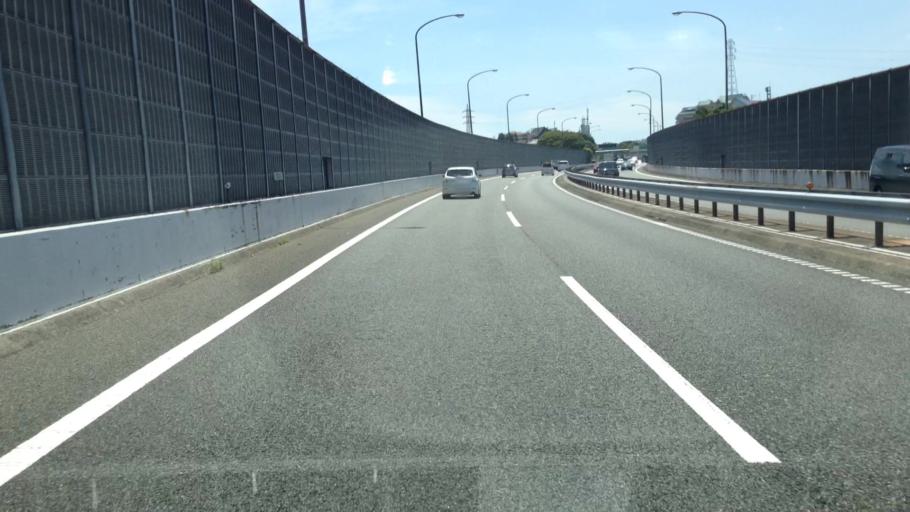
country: JP
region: Kanagawa
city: Yokohama
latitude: 35.4277
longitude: 139.5827
